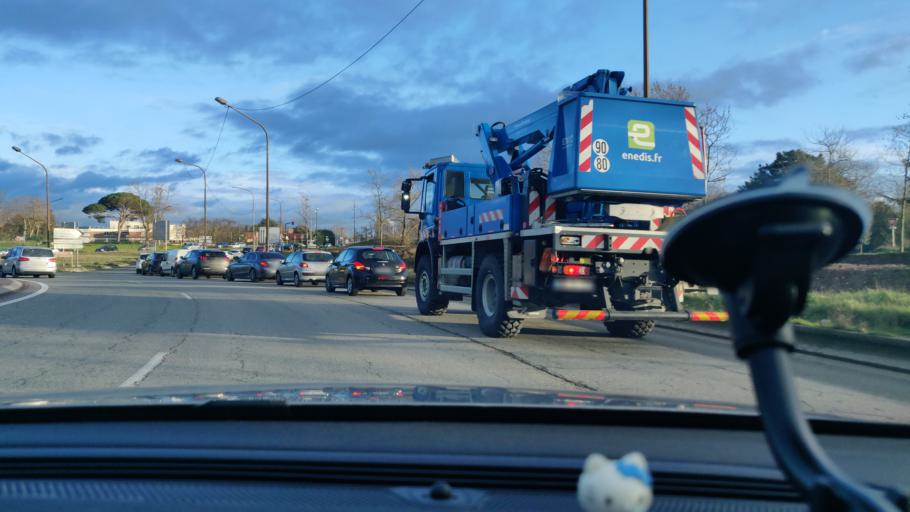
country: FR
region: Midi-Pyrenees
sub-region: Departement de la Haute-Garonne
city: Cugnaux
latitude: 43.5688
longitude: 1.3743
